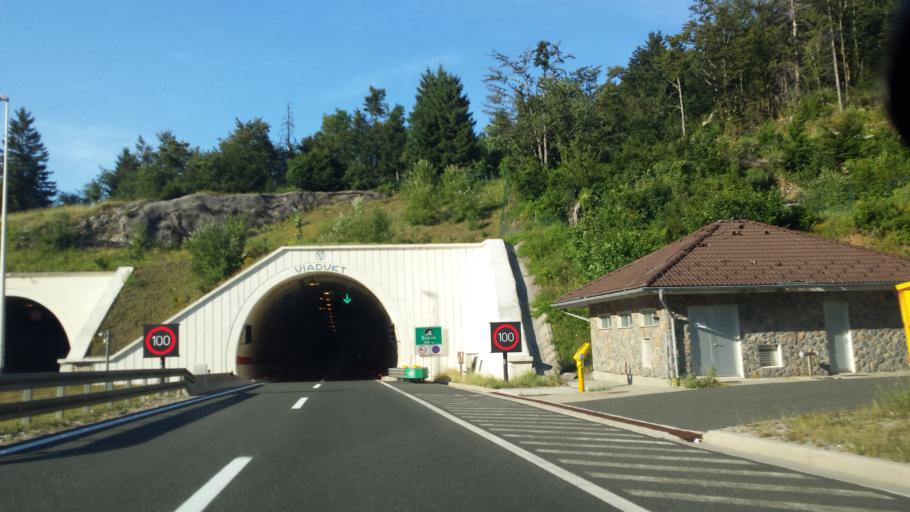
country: HR
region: Primorsko-Goranska
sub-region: Grad Delnice
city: Delnice
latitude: 45.3638
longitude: 14.7687
